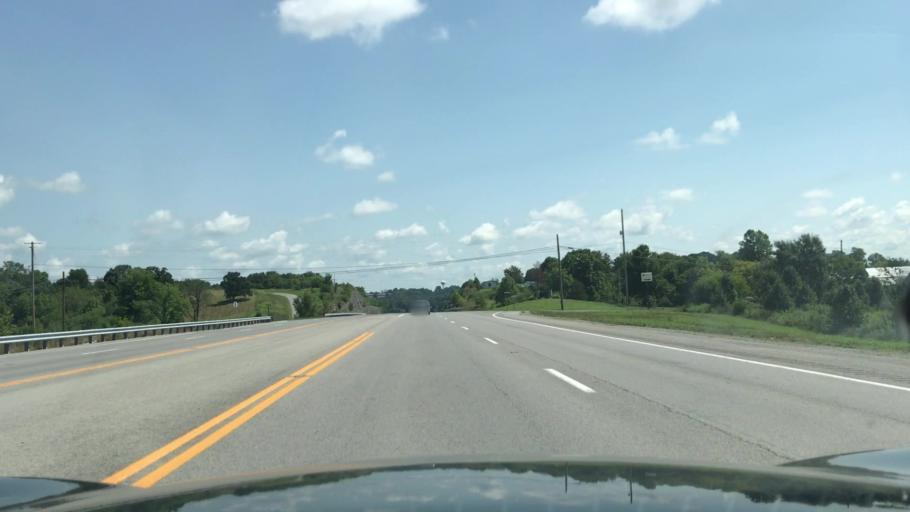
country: US
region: Kentucky
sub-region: Adair County
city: Columbia
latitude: 37.0806
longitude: -85.3327
